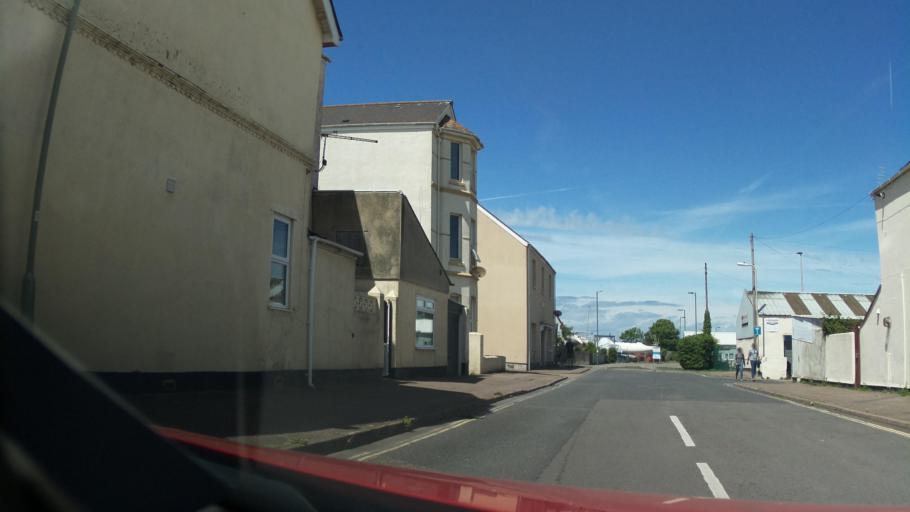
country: GB
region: England
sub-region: Devon
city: Exmouth
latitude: 50.6181
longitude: -3.4198
